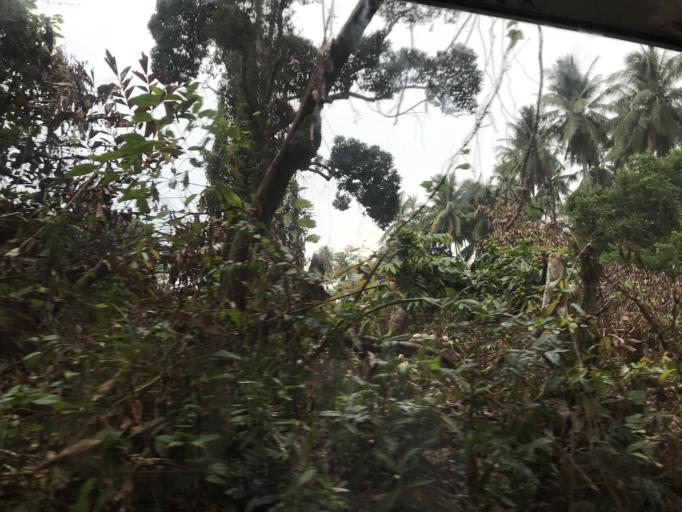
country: MY
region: Kelantan
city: Tumpat
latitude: 6.1675
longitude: 102.2010
